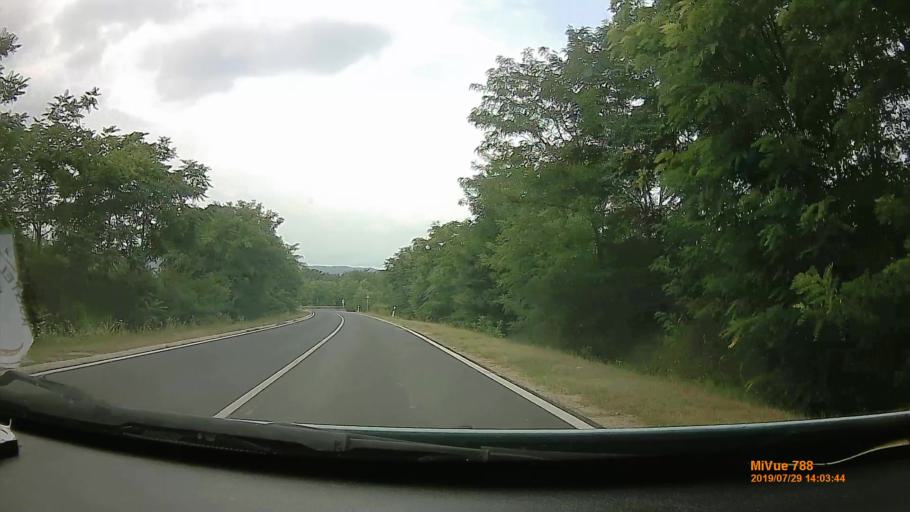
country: HU
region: Somogy
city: Balatonfoldvar
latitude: 46.8138
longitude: 17.9219
